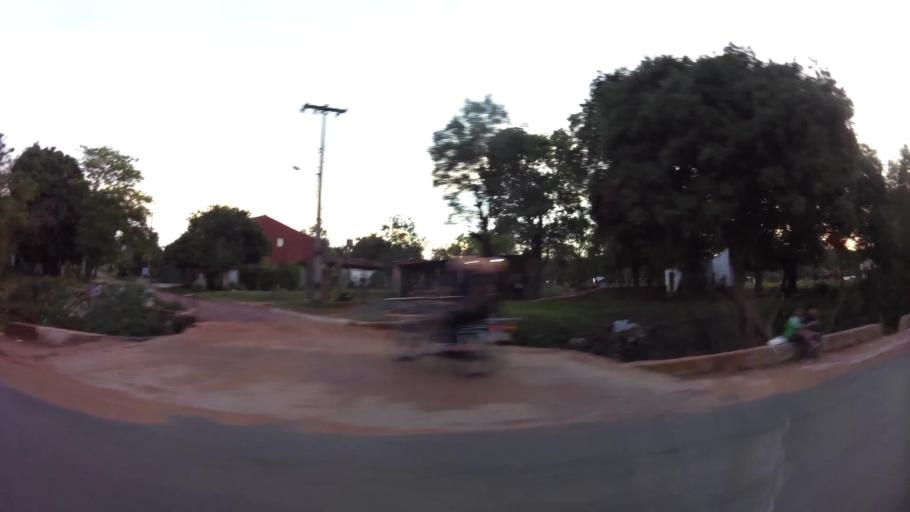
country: PY
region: Central
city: Nemby
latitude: -25.3936
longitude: -57.5205
